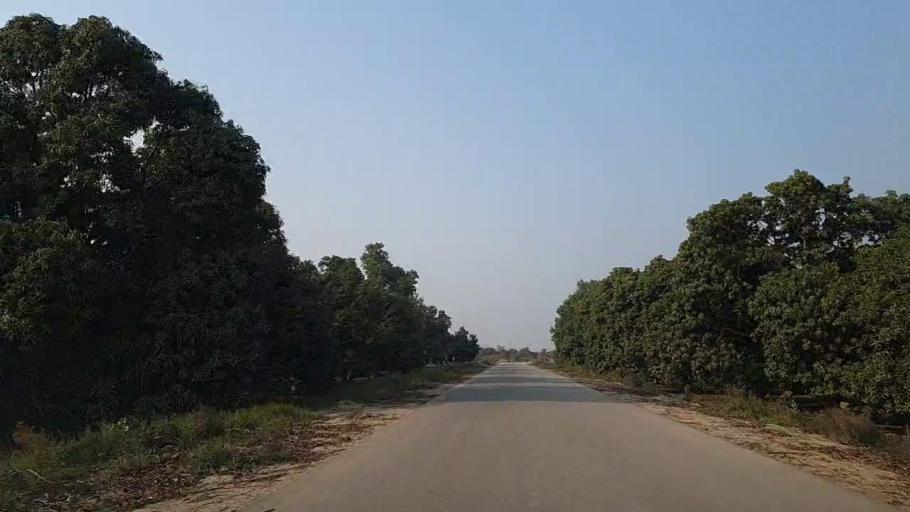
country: PK
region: Sindh
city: Sann
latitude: 26.1095
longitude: 68.1504
